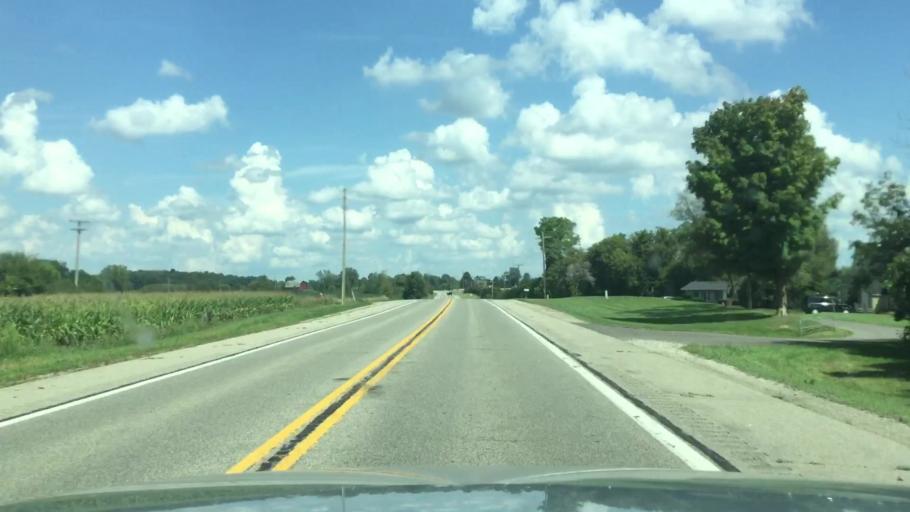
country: US
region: Michigan
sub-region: Lenawee County
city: Clinton
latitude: 42.0797
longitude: -83.9564
